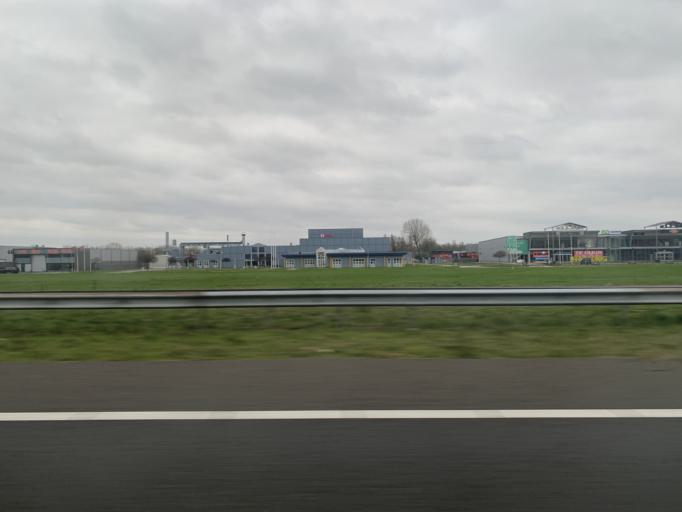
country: NL
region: Groningen
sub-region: Gemeente Leek
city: Leek
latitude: 53.1828
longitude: 6.3726
